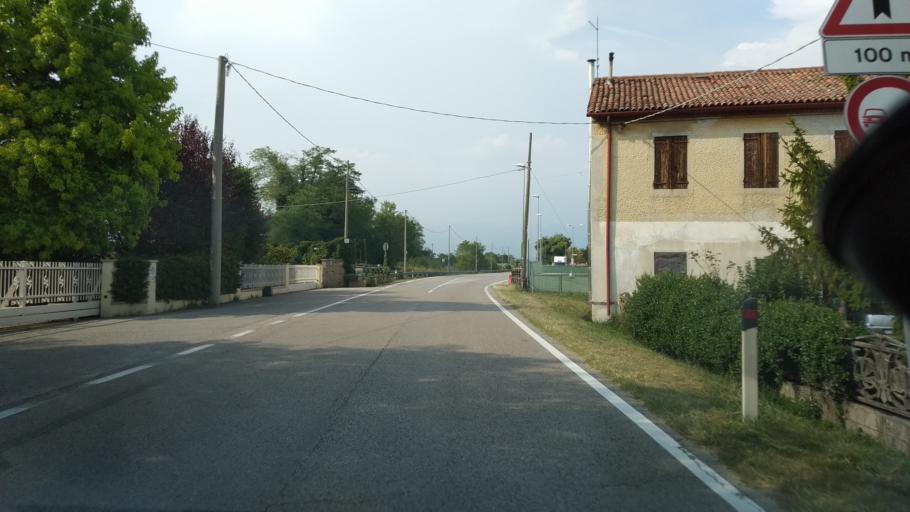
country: IT
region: Veneto
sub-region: Provincia di Vicenza
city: Tezze
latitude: 45.6713
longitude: 11.7106
